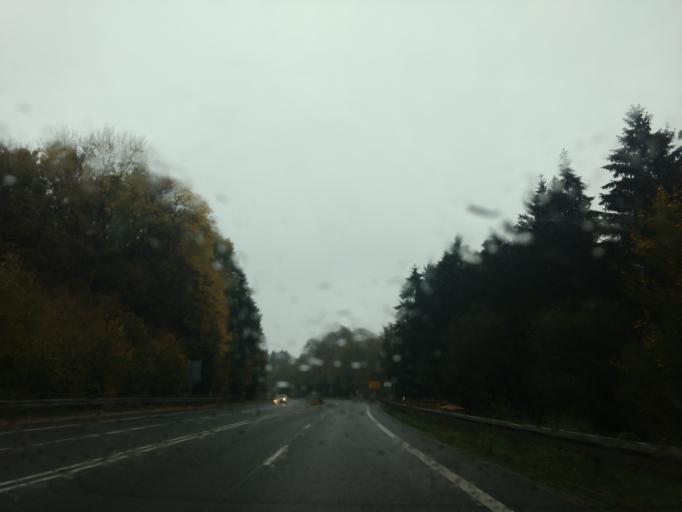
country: DE
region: Lower Saxony
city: Bad Iburg
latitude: 52.1740
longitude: 8.0642
